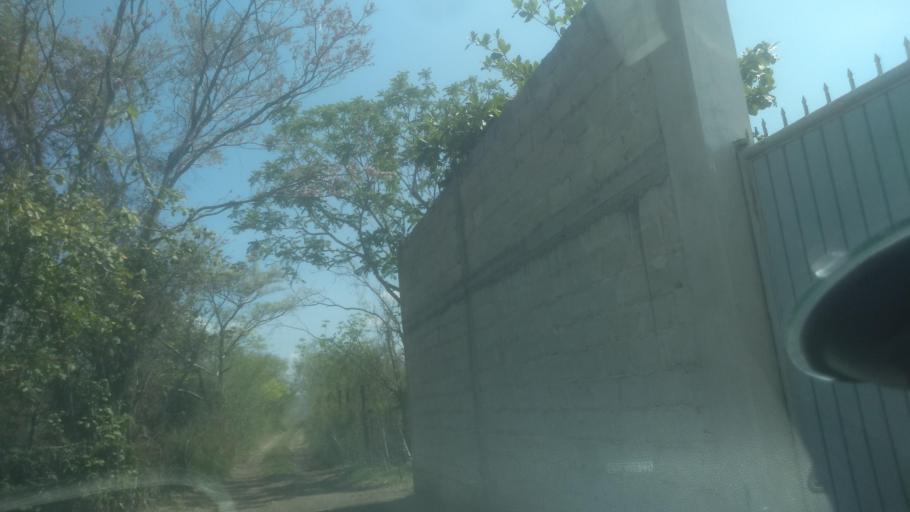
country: MX
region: Veracruz
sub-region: Emiliano Zapata
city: Plan del Rio
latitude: 19.3932
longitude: -96.6296
